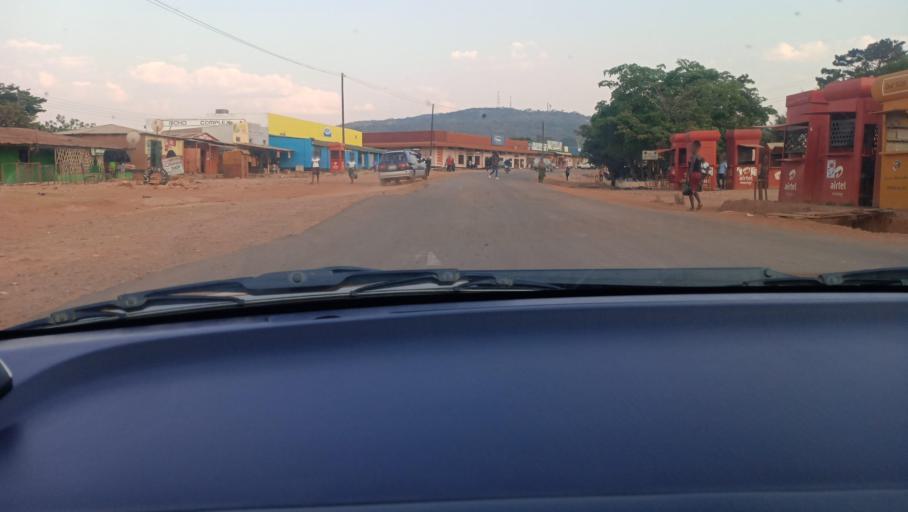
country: ZM
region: Northern
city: Mpika
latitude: -11.8362
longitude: 31.4469
